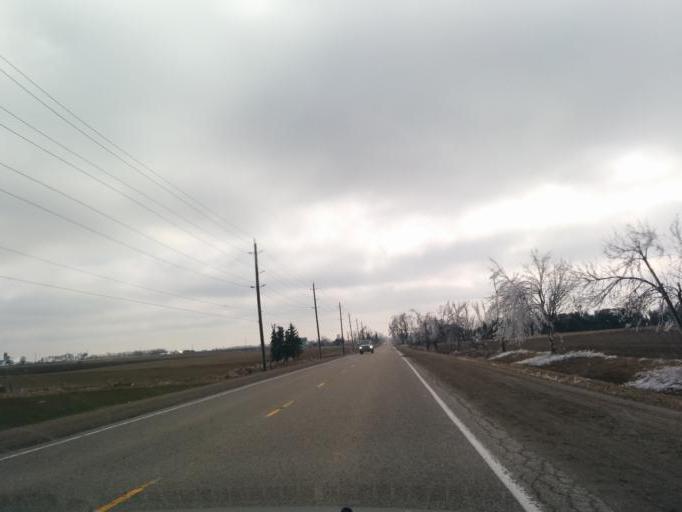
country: CA
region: Ontario
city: Waterloo
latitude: 43.6290
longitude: -80.5507
